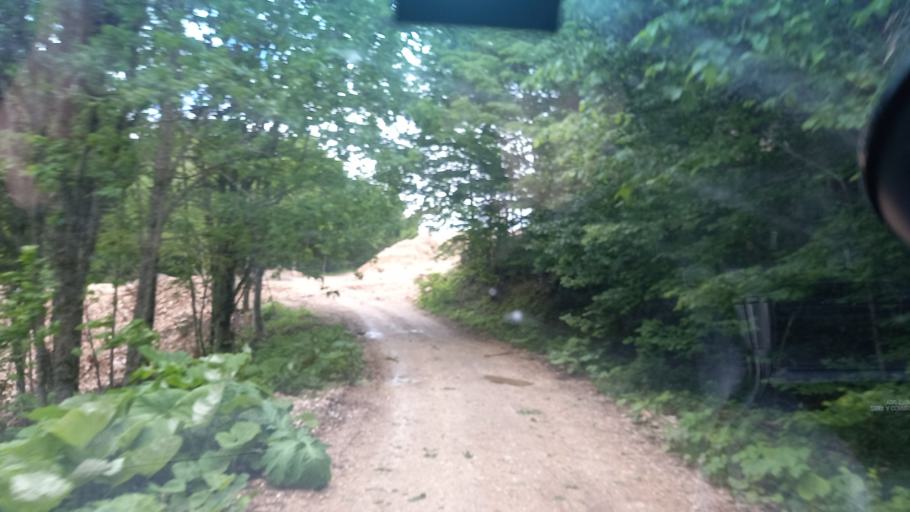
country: RU
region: Krasnodarskiy
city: Neftegorsk
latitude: 44.0551
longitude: 39.8211
